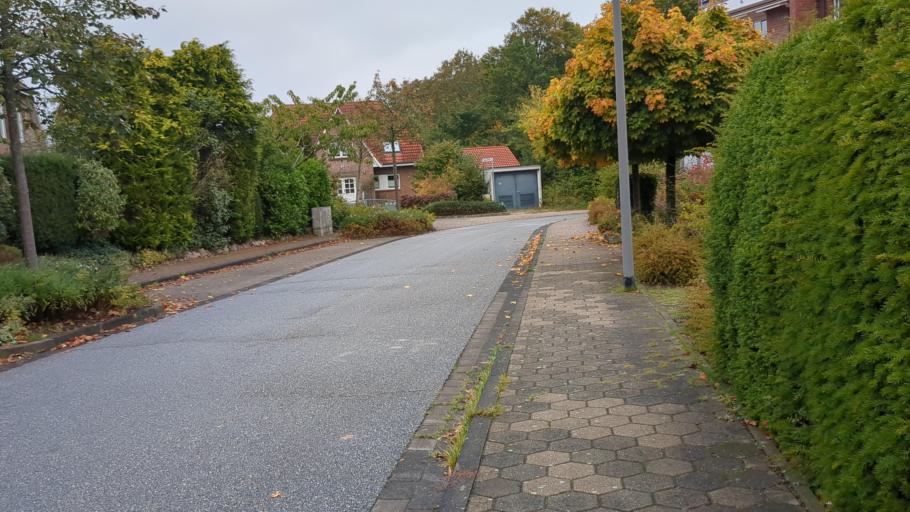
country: DE
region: Schleswig-Holstein
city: Wees
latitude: 54.8205
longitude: 9.4802
